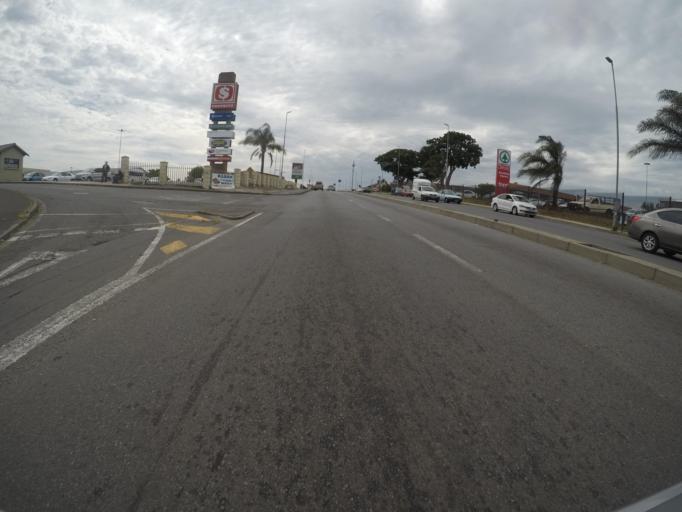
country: ZA
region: Eastern Cape
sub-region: Buffalo City Metropolitan Municipality
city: East London
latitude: -32.9937
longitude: 27.8680
